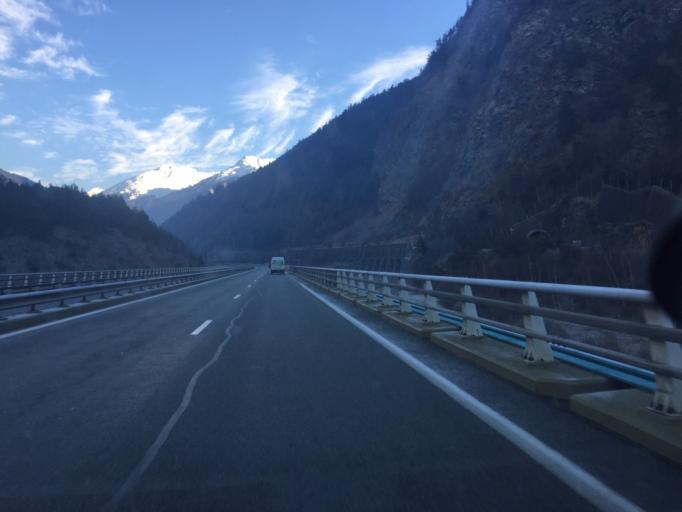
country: FR
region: Rhone-Alpes
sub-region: Departement de la Savoie
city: Modane
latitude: 45.2005
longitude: 6.5982
